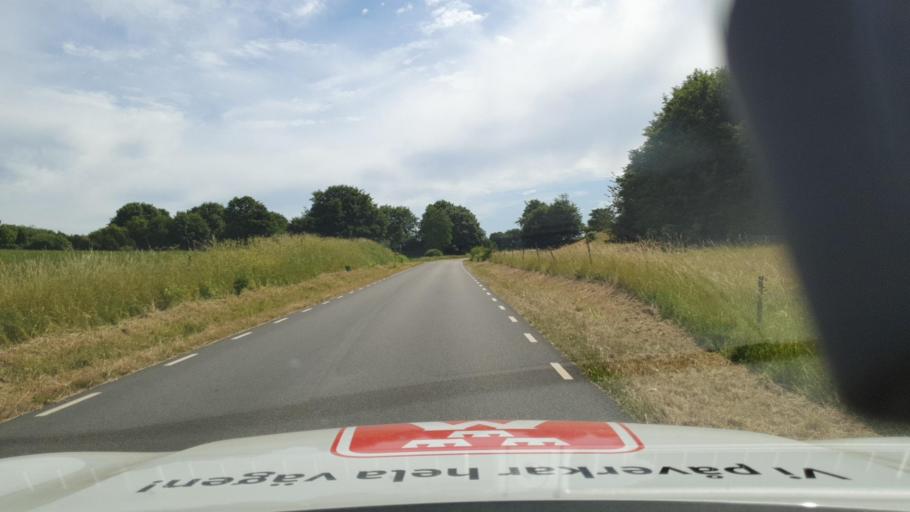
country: SE
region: Skane
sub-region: Tomelilla Kommun
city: Tomelilla
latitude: 55.6827
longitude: 13.9412
